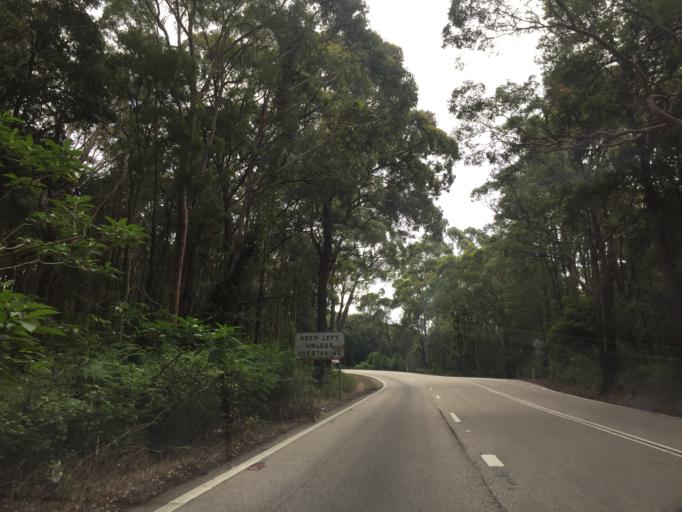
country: AU
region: New South Wales
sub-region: Hawkesbury
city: Richmond
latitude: -33.5414
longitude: 150.6332
